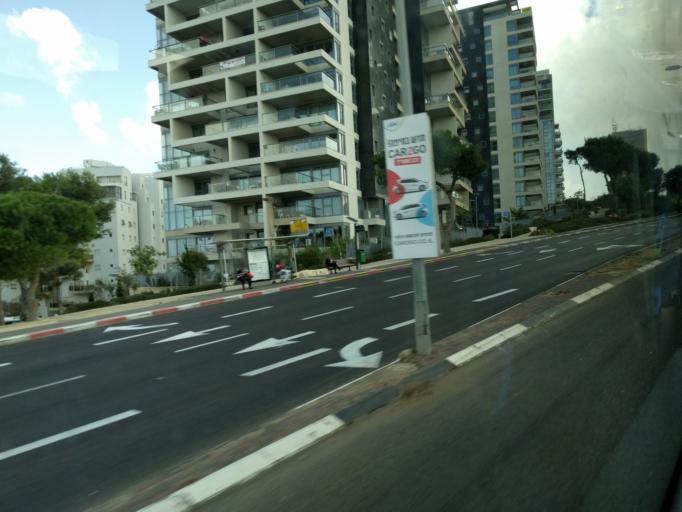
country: IL
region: Haifa
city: Nesher
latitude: 32.7668
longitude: 35.0117
